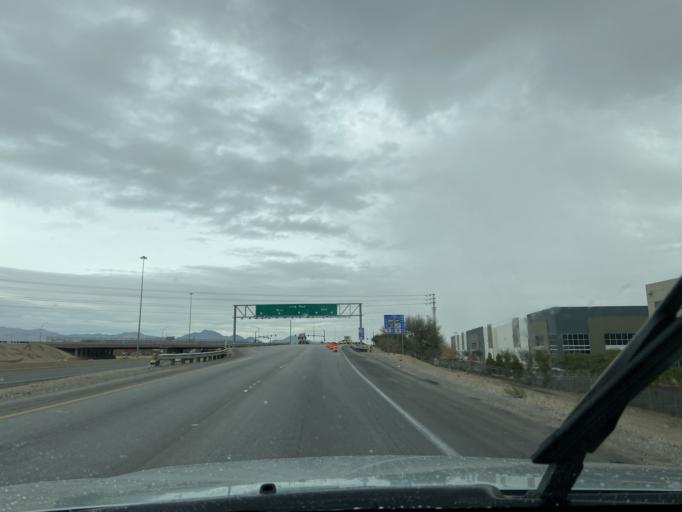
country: US
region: Nevada
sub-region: Clark County
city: Sunrise Manor
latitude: 36.2382
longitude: -115.1037
